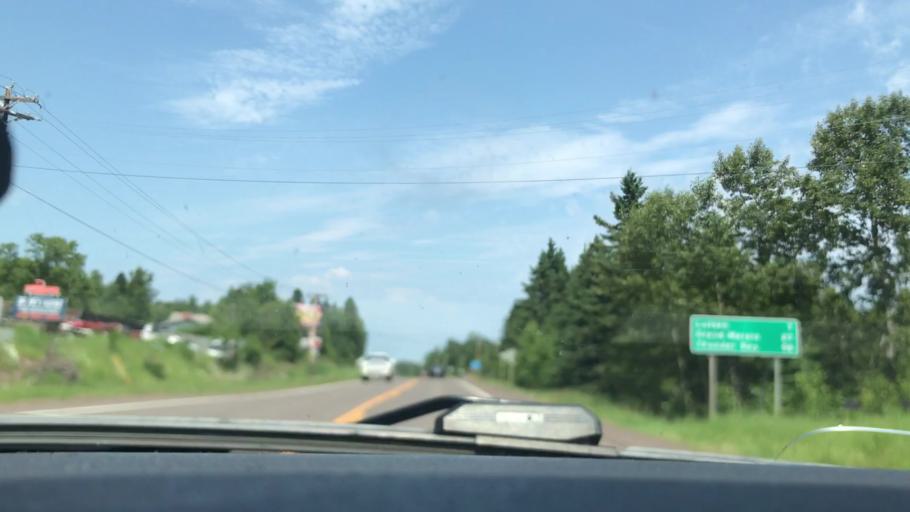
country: US
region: Minnesota
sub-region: Lake County
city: Silver Bay
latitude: 47.5771
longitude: -90.8299
